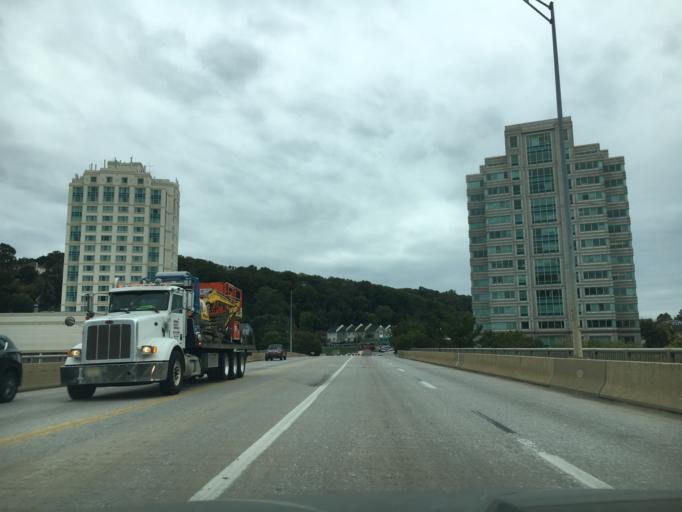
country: US
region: Pennsylvania
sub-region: Montgomery County
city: West Conshohocken
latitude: 40.0706
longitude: -75.3096
